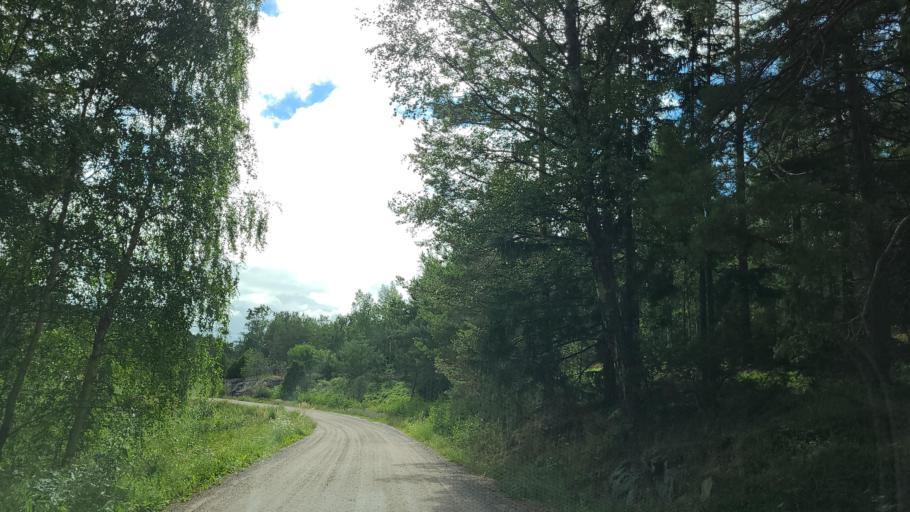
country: FI
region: Varsinais-Suomi
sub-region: Aboland-Turunmaa
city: Nagu
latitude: 60.1936
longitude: 21.7645
